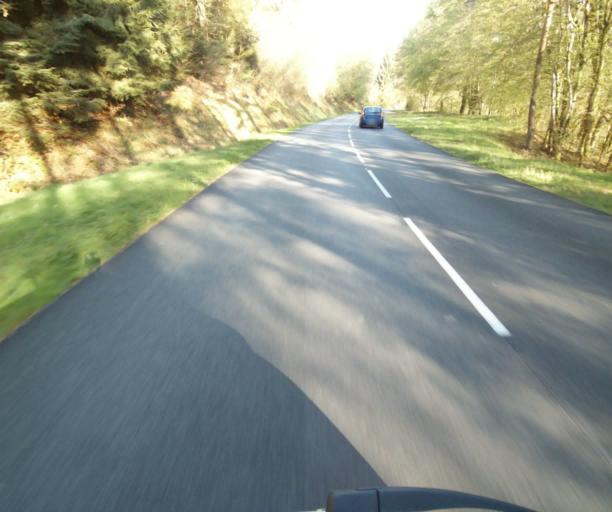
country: FR
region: Limousin
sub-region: Departement de la Correze
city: Correze
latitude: 45.3560
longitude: 1.8751
